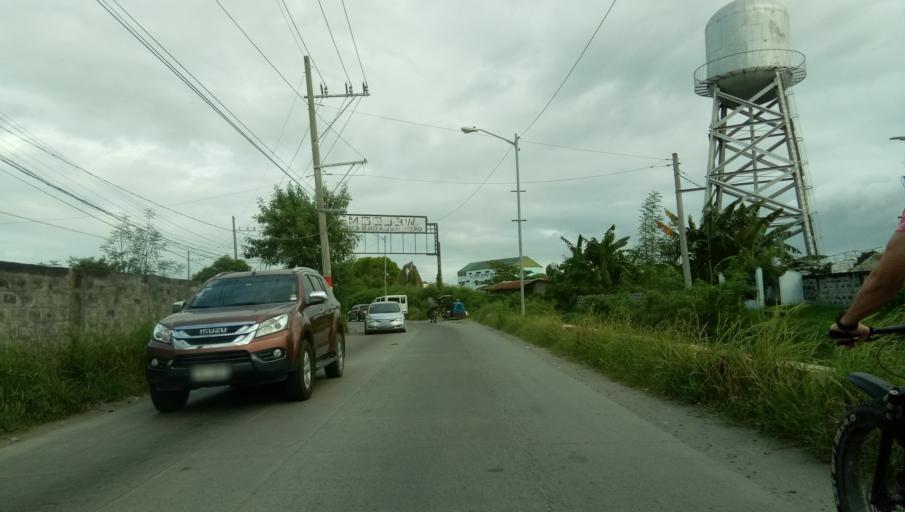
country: PH
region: Calabarzon
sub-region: Province of Cavite
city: Dasmarinas
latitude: 14.3676
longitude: 120.9284
